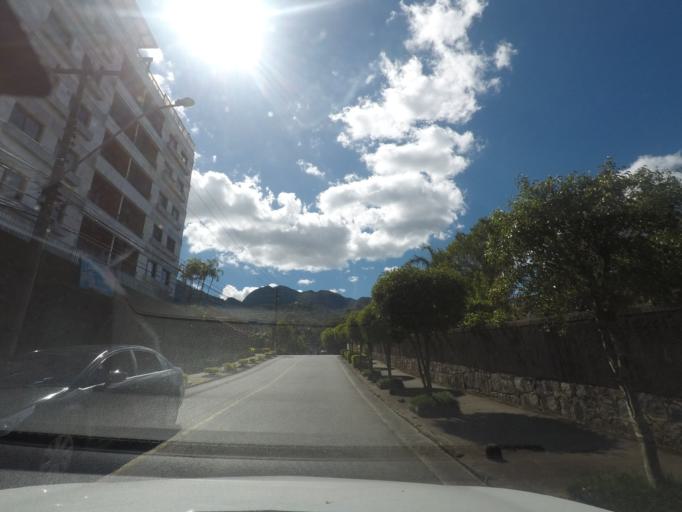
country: BR
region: Rio de Janeiro
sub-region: Teresopolis
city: Teresopolis
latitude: -22.4448
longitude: -42.9797
